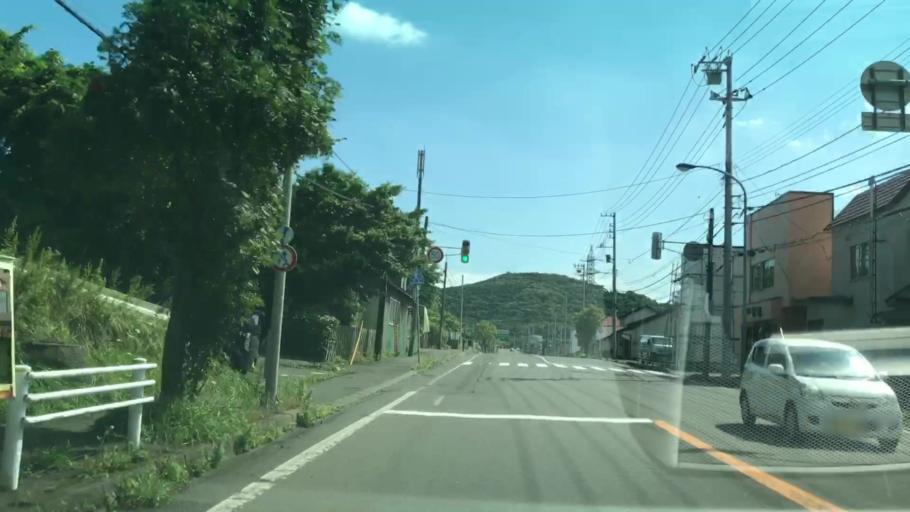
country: JP
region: Hokkaido
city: Muroran
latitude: 42.3267
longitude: 140.9963
